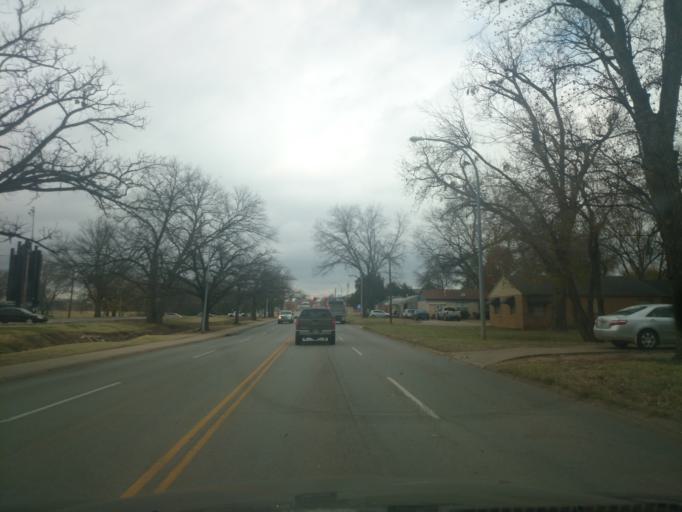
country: US
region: Oklahoma
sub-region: Payne County
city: Stillwater
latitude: 36.1291
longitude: -97.0627
